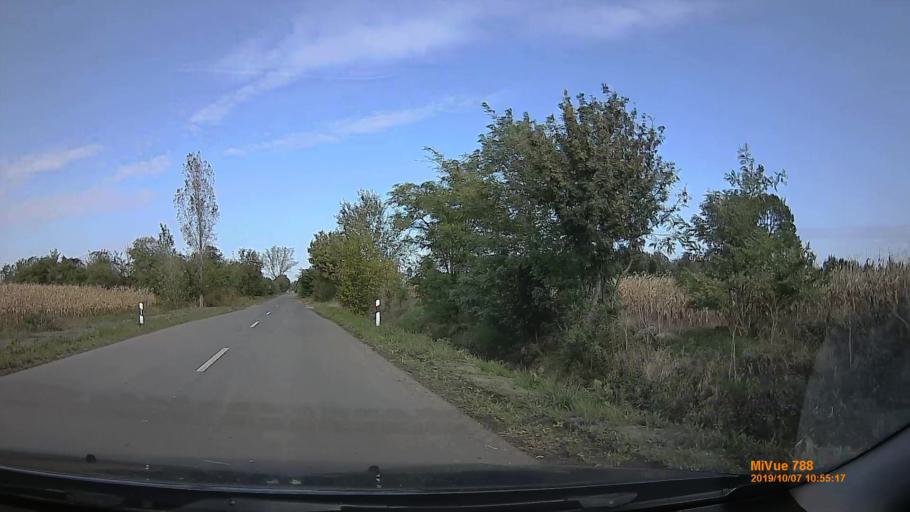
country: HU
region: Bekes
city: Kondoros
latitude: 46.7422
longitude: 20.8055
